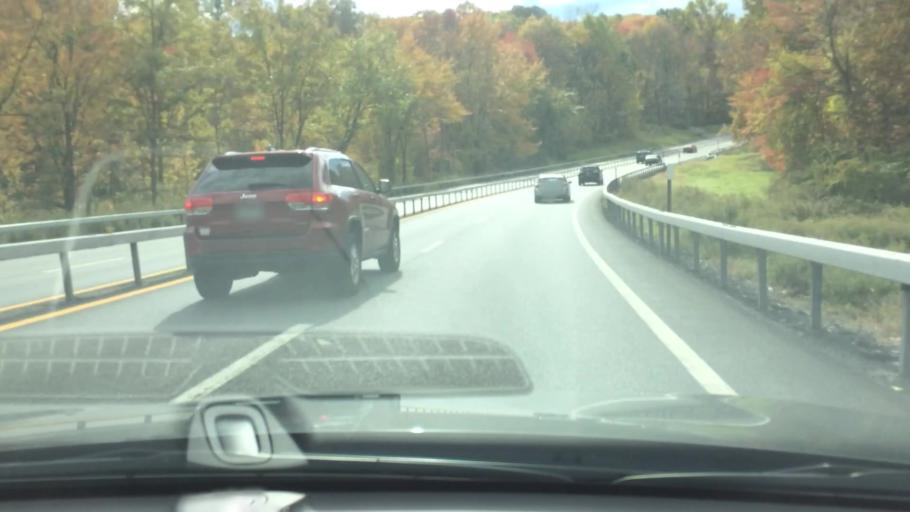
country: US
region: New York
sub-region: Dutchess County
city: Brinckerhoff
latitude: 41.5009
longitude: -73.7957
